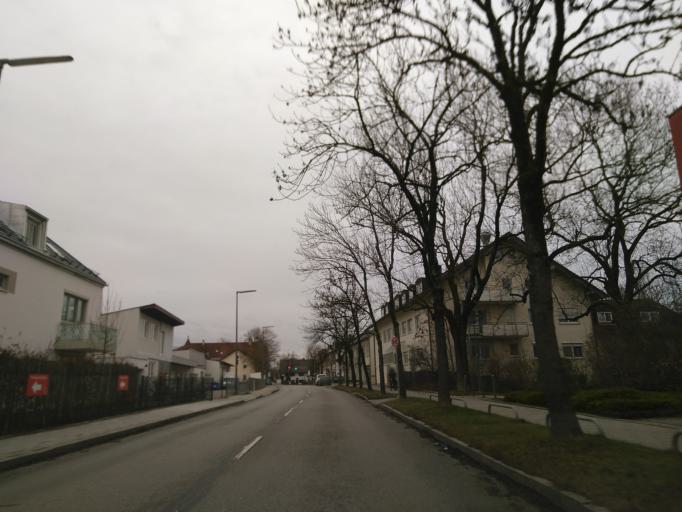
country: DE
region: Bavaria
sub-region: Upper Bavaria
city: Neubiberg
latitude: 48.1274
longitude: 11.6749
